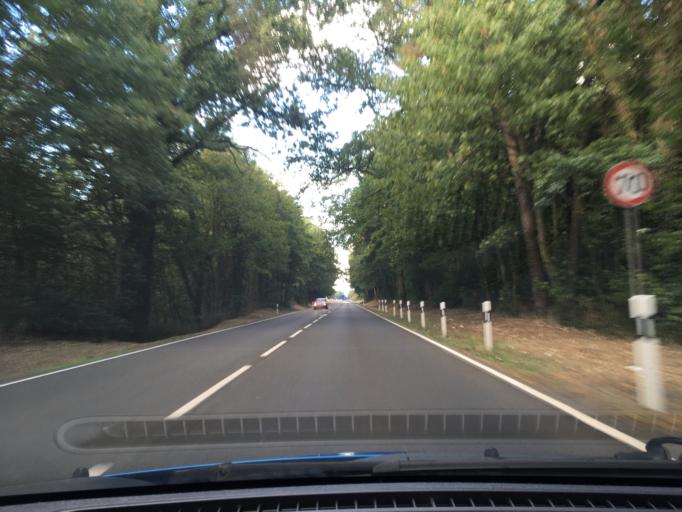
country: DE
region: Mecklenburg-Vorpommern
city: Ludwigslust
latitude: 53.3380
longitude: 11.5111
